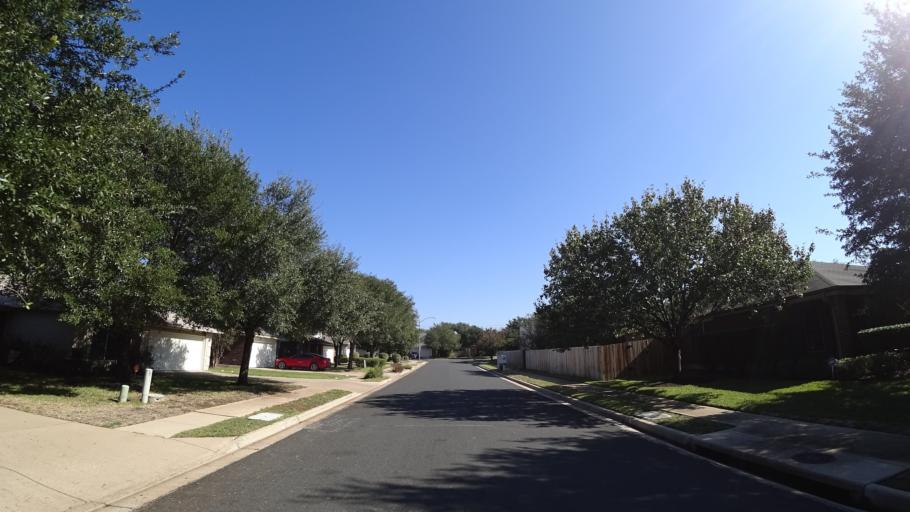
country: US
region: Texas
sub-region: Travis County
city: Shady Hollow
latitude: 30.1995
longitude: -97.8551
